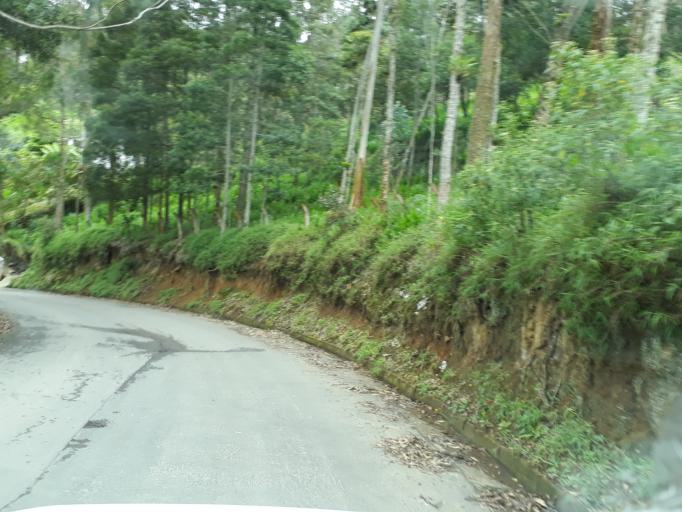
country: CO
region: Cundinamarca
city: Junin
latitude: 4.8169
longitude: -73.6754
